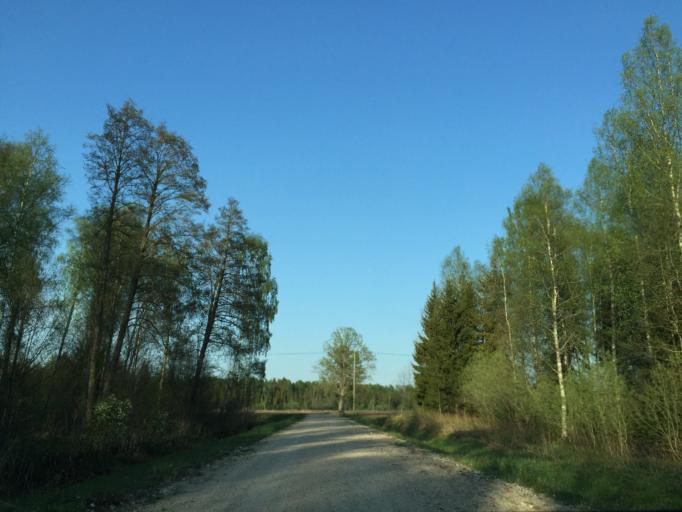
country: LV
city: Tireli
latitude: 56.8382
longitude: 23.7161
